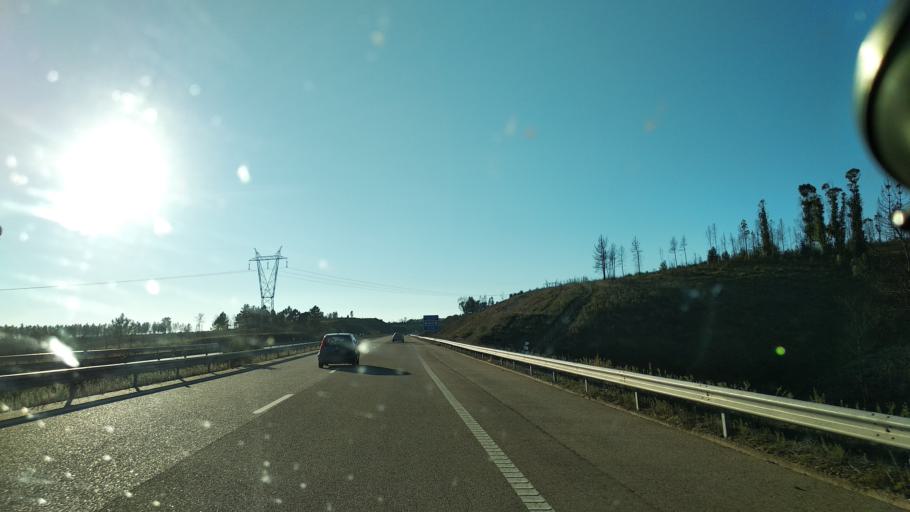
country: PT
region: Santarem
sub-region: Macao
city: Macao
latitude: 39.4948
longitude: -8.0521
